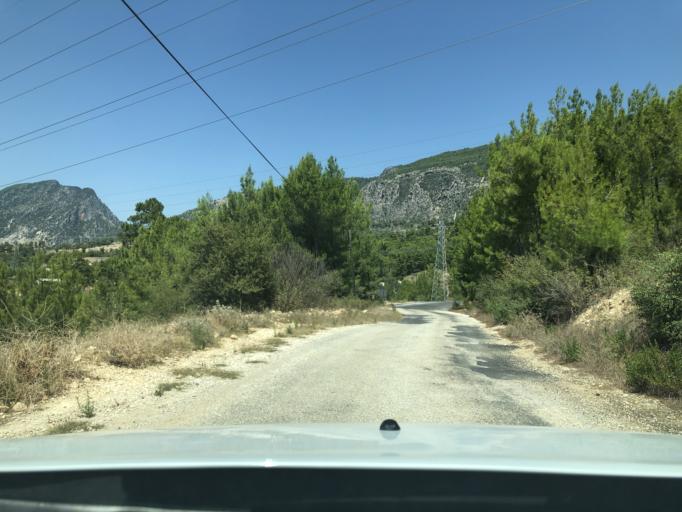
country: TR
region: Antalya
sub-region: Manavgat
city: Manavgat
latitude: 36.8752
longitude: 31.5497
